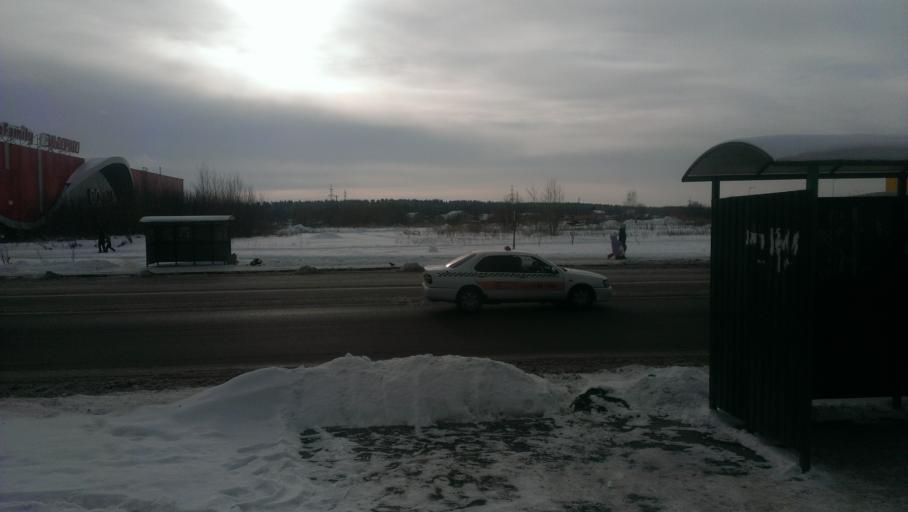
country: RU
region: Altai Krai
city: Novosilikatnyy
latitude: 53.3277
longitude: 83.6890
